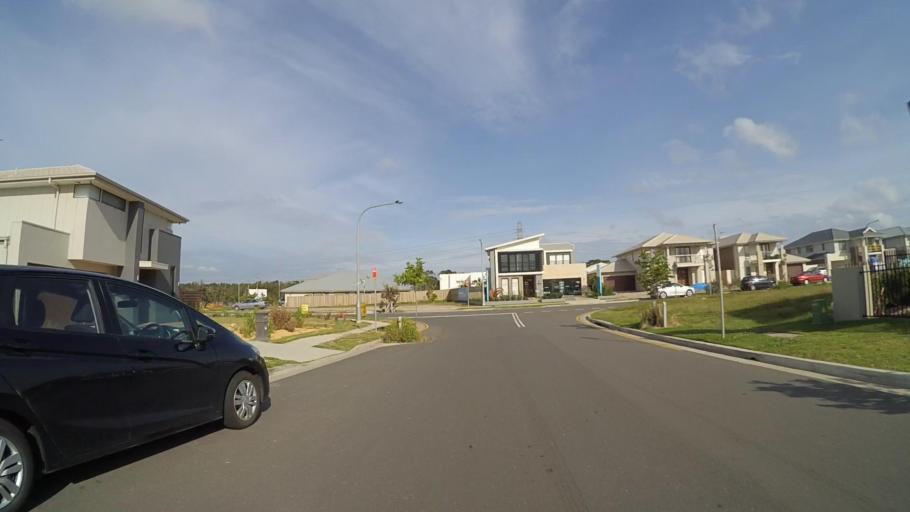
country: AU
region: New South Wales
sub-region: Sutherland Shire
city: Cronulla
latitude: -34.0364
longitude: 151.1619
